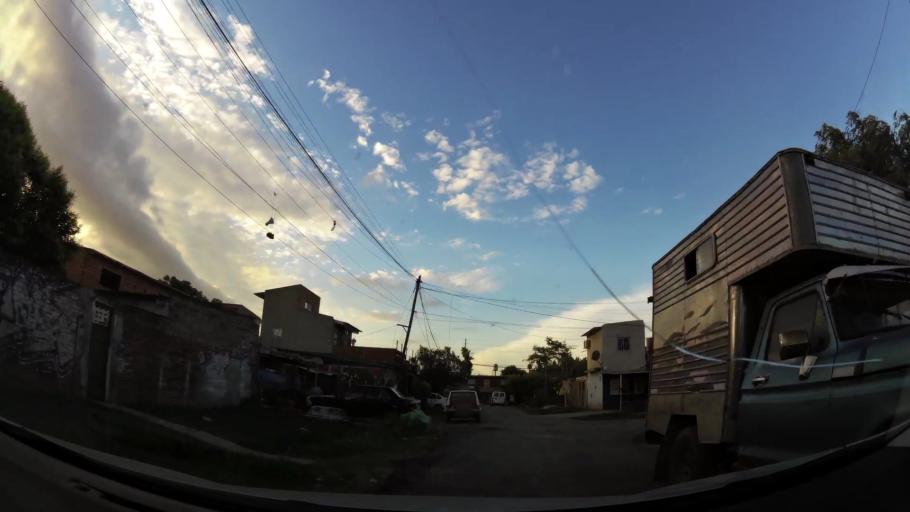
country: AR
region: Buenos Aires
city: Santa Catalina - Dique Lujan
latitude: -34.4365
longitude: -58.6701
